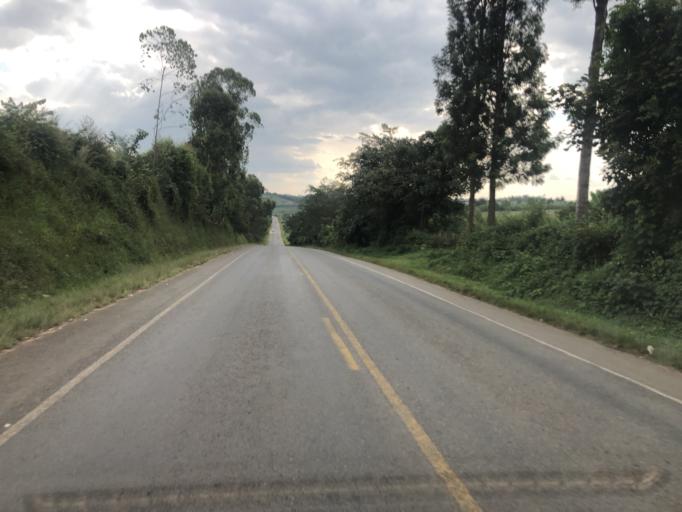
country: UG
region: Western Region
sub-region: Sheema District
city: Kibingo
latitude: -0.5613
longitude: 30.3365
